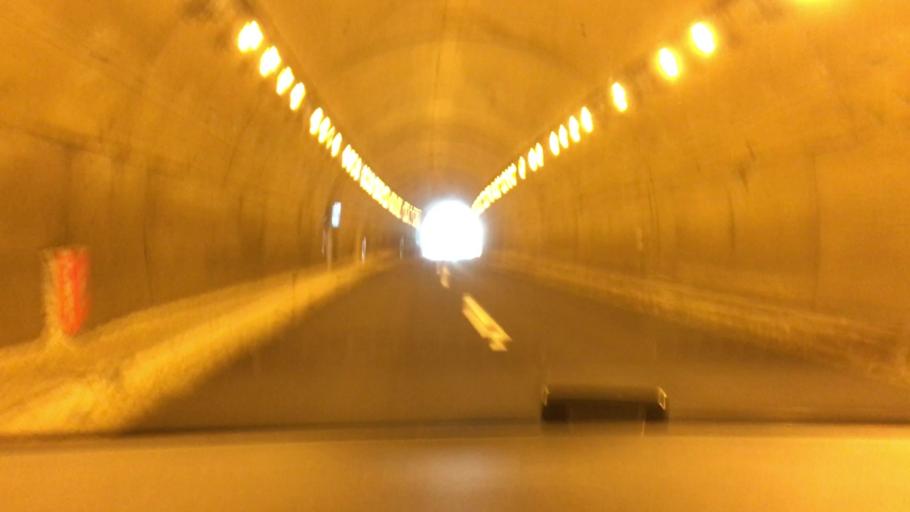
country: JP
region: Akita
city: Hanawa
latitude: 40.1153
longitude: 140.8882
